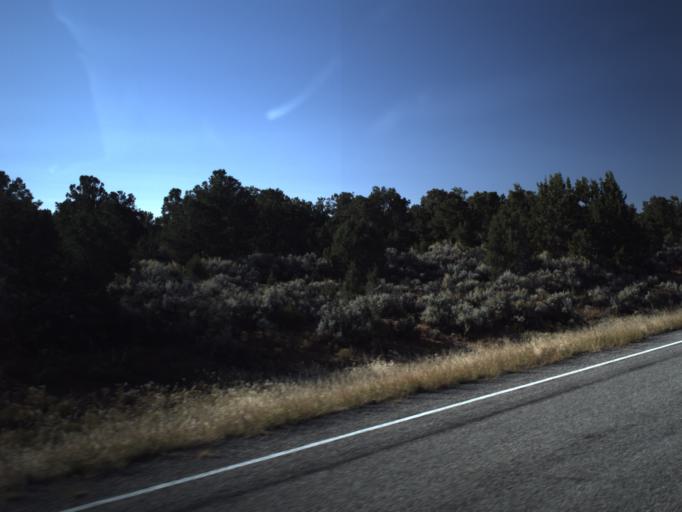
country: US
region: Utah
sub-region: San Juan County
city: Blanding
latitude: 37.5519
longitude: -109.9385
